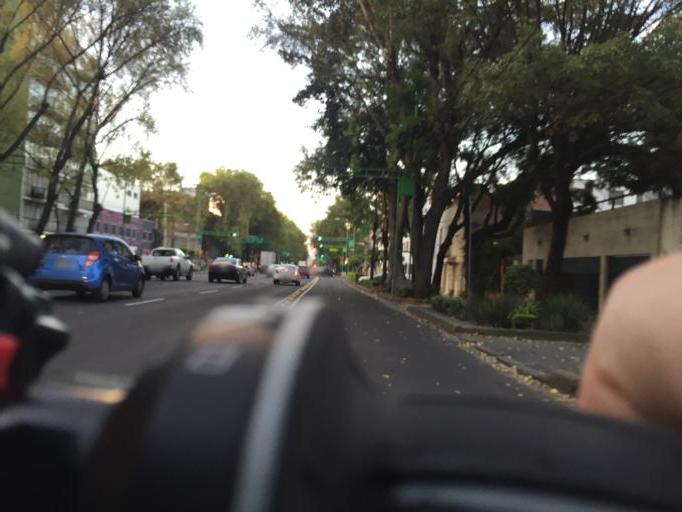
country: MX
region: Mexico City
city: Benito Juarez
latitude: 19.4002
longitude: -99.1454
